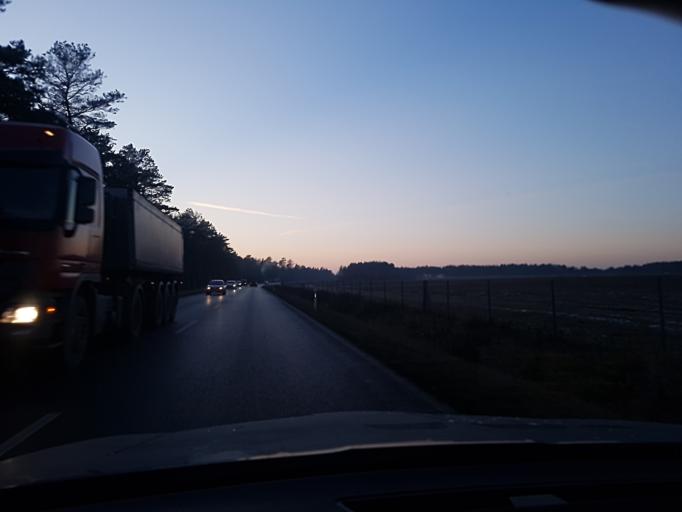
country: DE
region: Brandenburg
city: Finsterwalde
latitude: 51.6329
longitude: 13.6726
